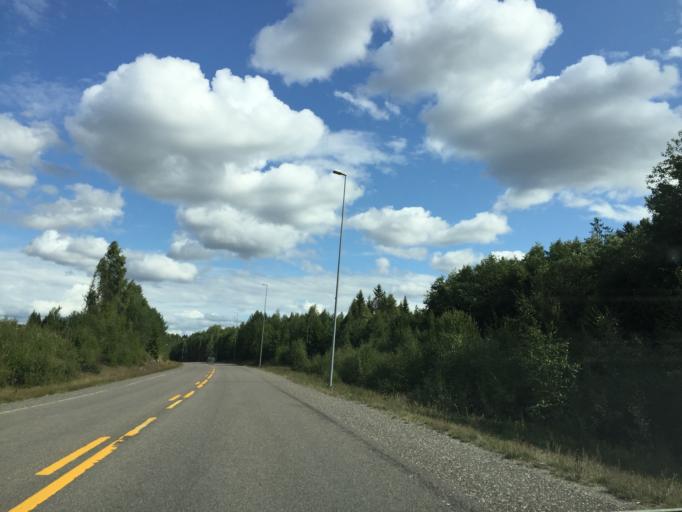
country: NO
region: Ostfold
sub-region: Hobol
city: Knappstad
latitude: 59.6168
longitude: 11.0402
